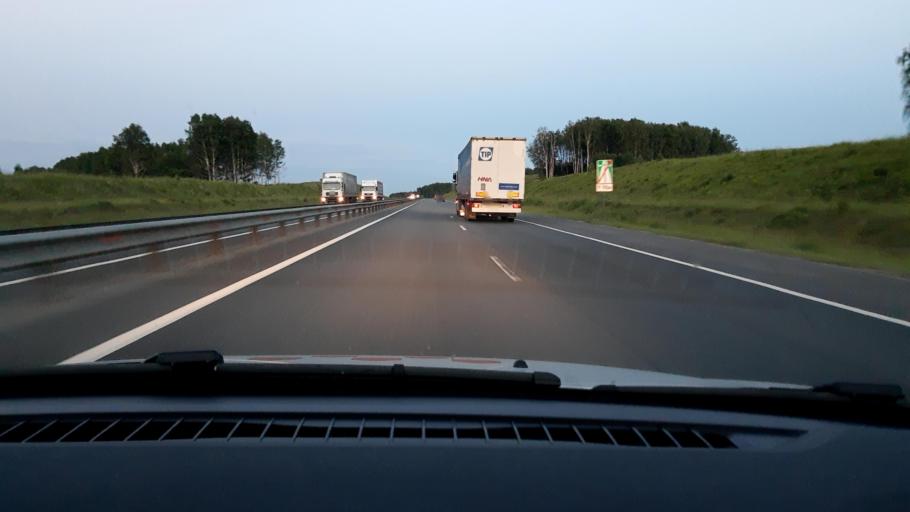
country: RU
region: Nizjnij Novgorod
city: Kstovo
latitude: 56.0748
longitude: 44.1063
